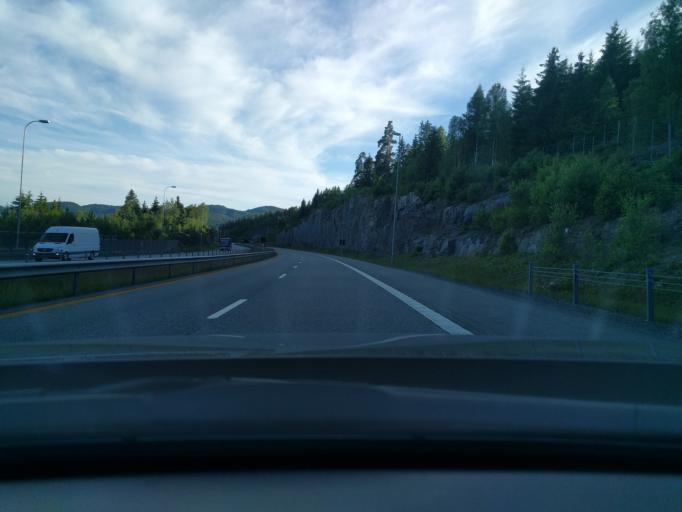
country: NO
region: Vestfold
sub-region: Sande
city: Sande
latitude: 59.6115
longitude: 10.1827
